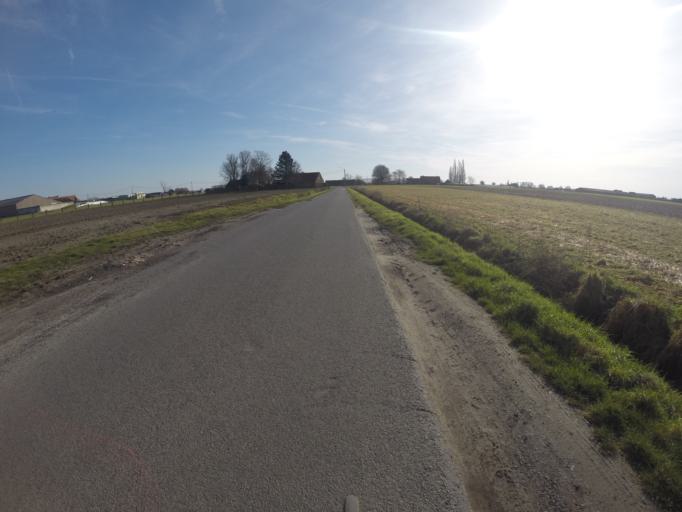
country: BE
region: Flanders
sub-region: Provincie West-Vlaanderen
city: Wingene
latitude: 51.0641
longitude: 3.3344
